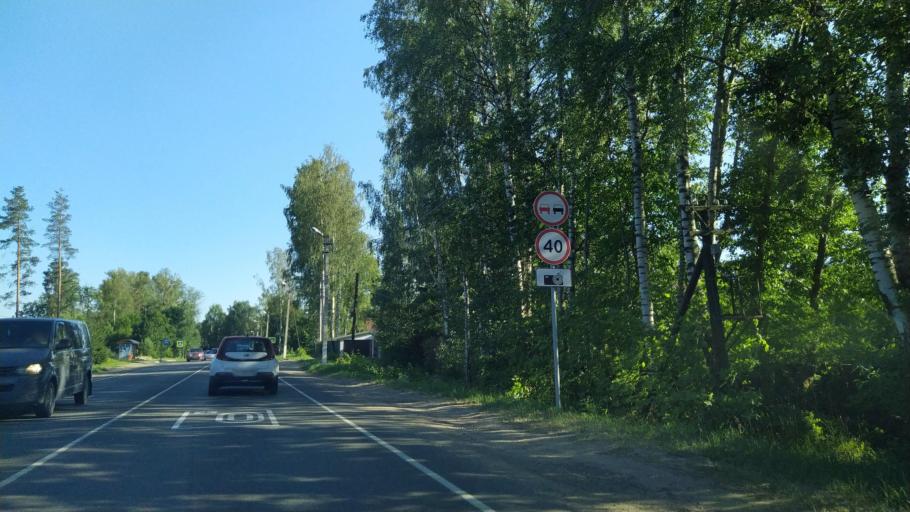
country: RU
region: Leningrad
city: Toksovo
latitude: 60.1497
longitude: 30.5225
